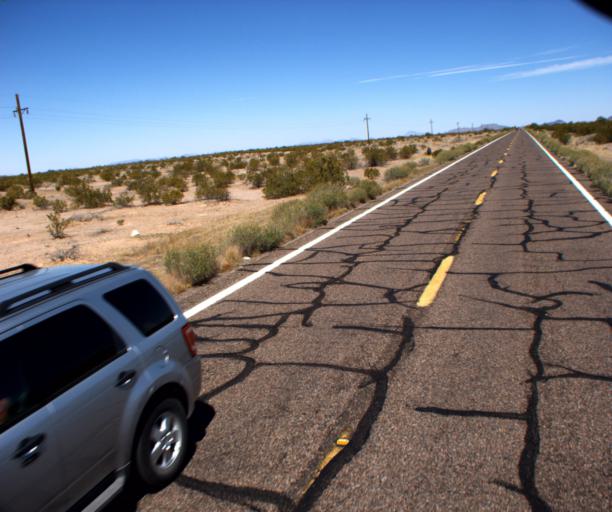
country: US
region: Arizona
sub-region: Pima County
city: Ajo
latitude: 32.6016
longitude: -112.8701
